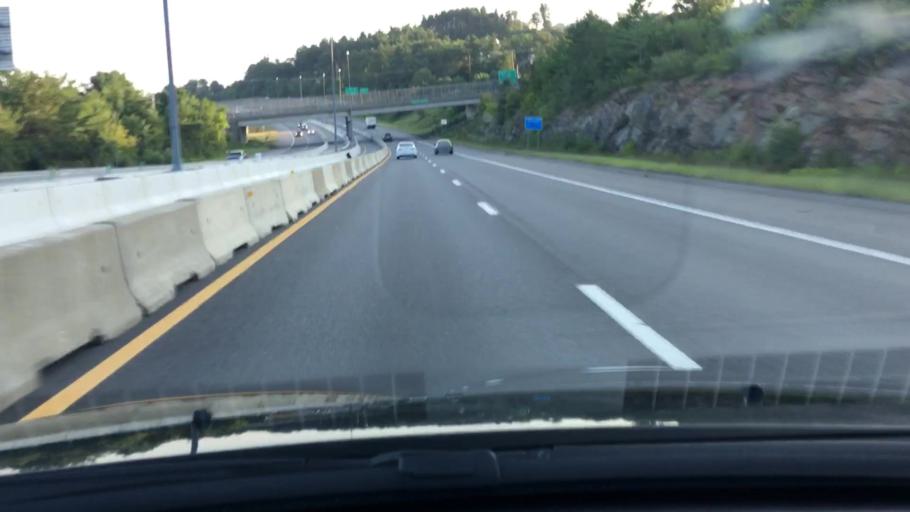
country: US
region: Massachusetts
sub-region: Worcester County
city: Worcester
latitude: 42.3161
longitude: -71.8058
